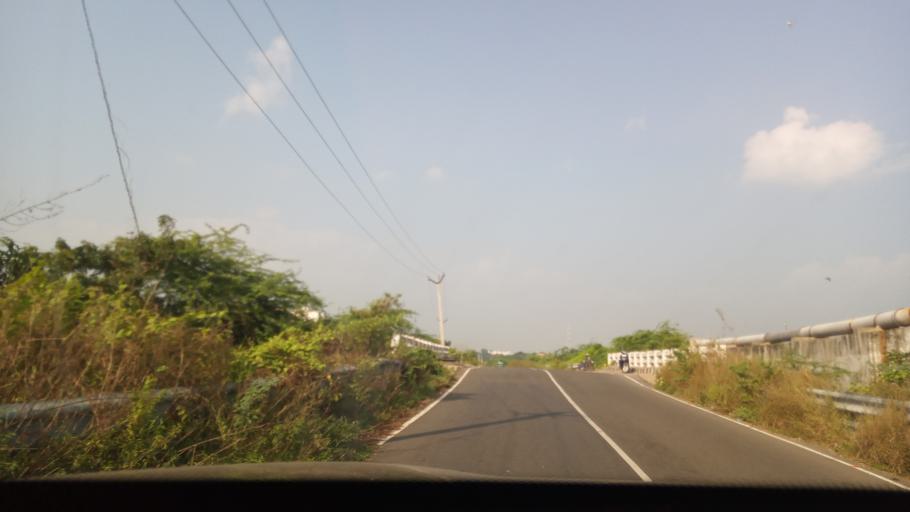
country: IN
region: Tamil Nadu
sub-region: Kancheepuram
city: Injambakkam
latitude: 12.7839
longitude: 80.2361
